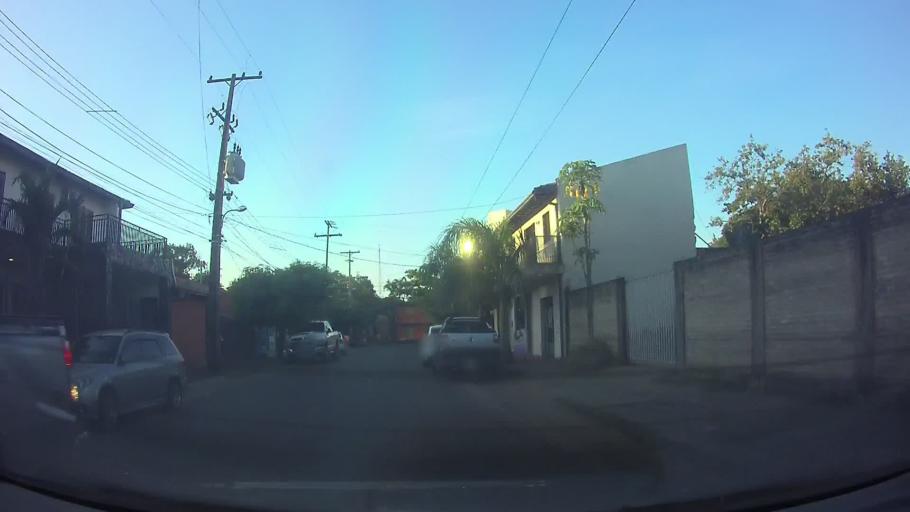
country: PY
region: Central
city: Fernando de la Mora
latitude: -25.2772
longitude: -57.5535
